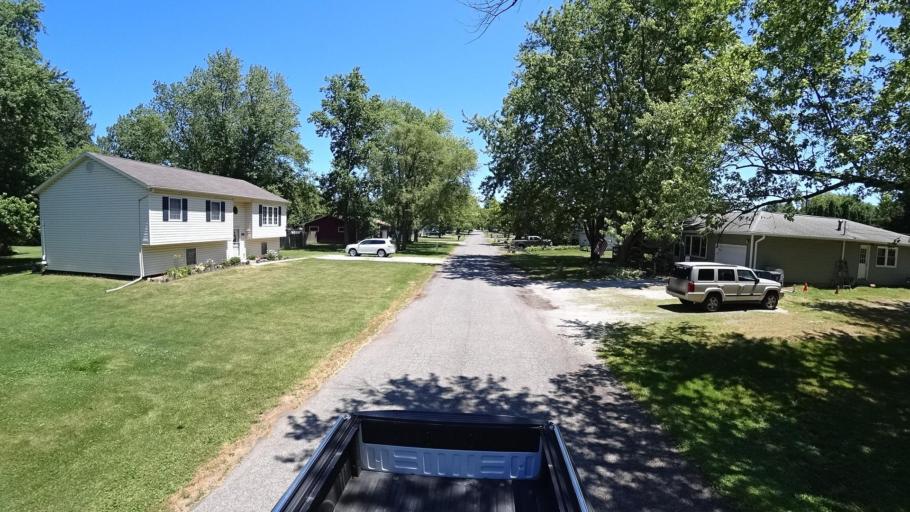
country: US
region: Indiana
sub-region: Porter County
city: Chesterton
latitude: 41.6177
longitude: -87.0572
